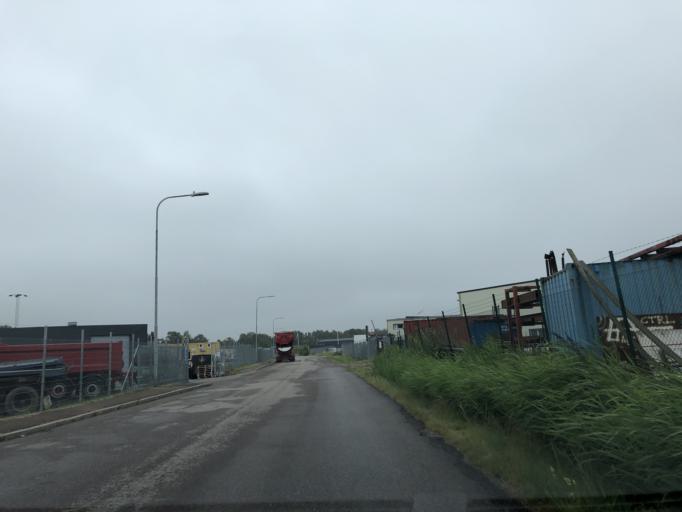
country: SE
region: Vaestra Goetaland
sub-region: Goteborg
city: Goeteborg
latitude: 57.7349
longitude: 11.9493
